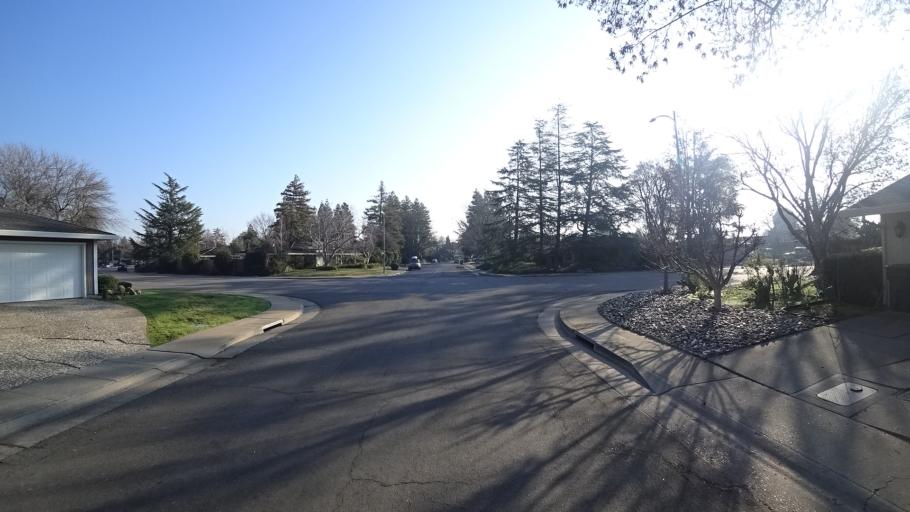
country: US
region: California
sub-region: Yolo County
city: Davis
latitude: 38.5553
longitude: -121.7924
